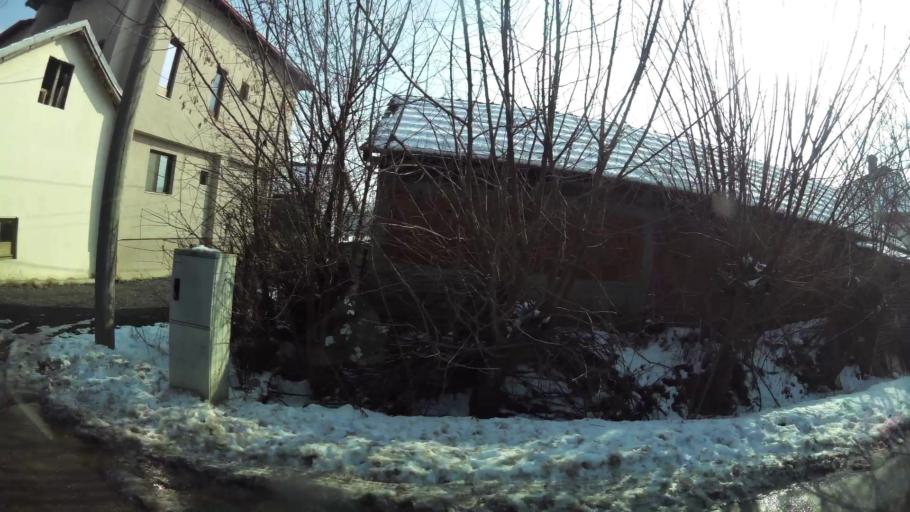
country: MK
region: Suto Orizari
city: Suto Orizare
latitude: 42.0274
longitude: 21.3815
